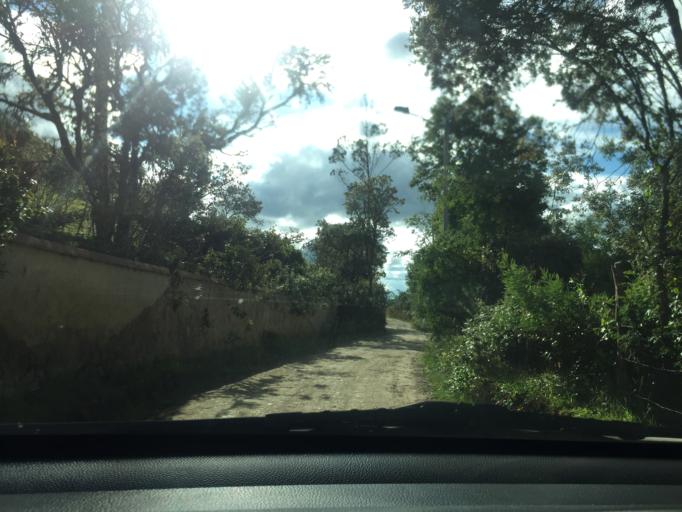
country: CO
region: Cundinamarca
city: Sopo
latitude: 4.9196
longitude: -73.9142
